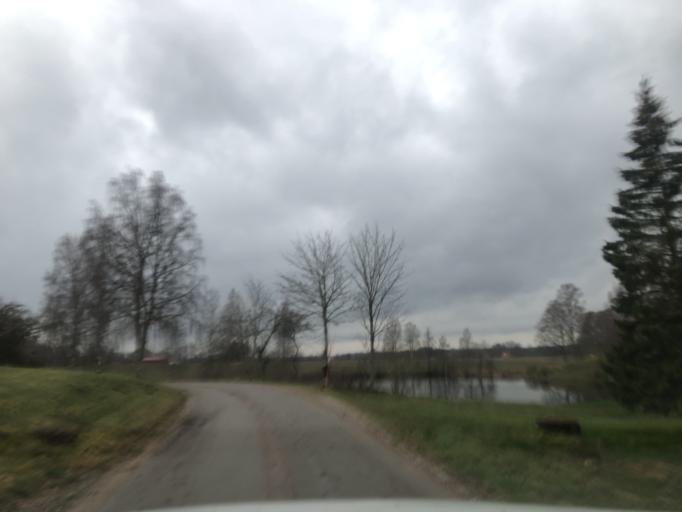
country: SE
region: Vaestra Goetaland
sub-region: Ulricehamns Kommun
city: Ulricehamn
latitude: 57.9046
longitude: 13.4848
